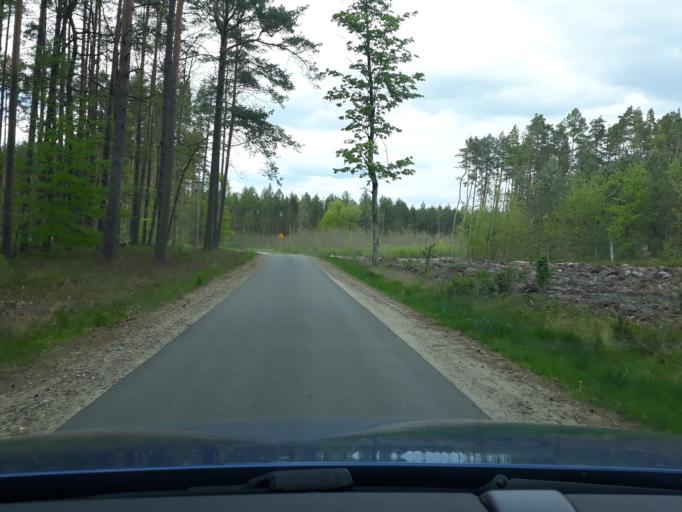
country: PL
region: Pomeranian Voivodeship
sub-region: Powiat czluchowski
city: Czluchow
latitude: 53.7330
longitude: 17.3444
